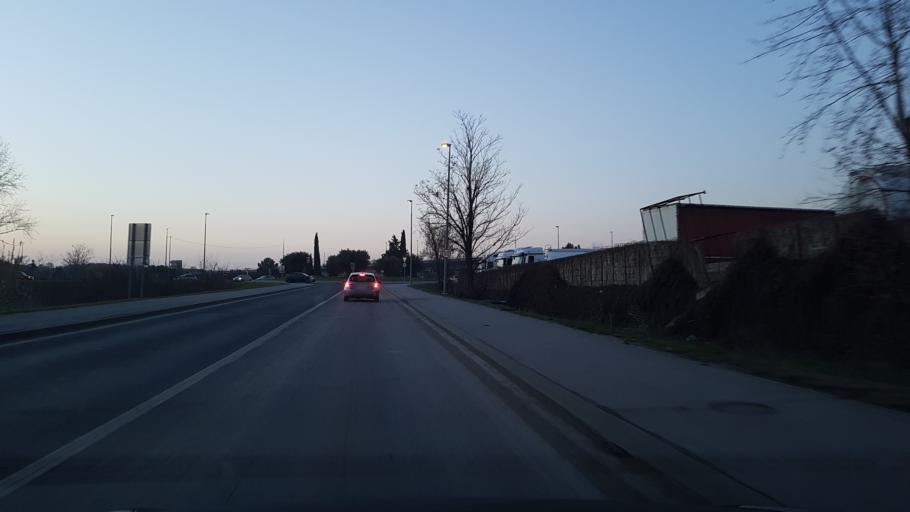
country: SI
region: Koper-Capodistria
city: Spodnje Skofije
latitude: 45.5573
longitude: 13.7878
